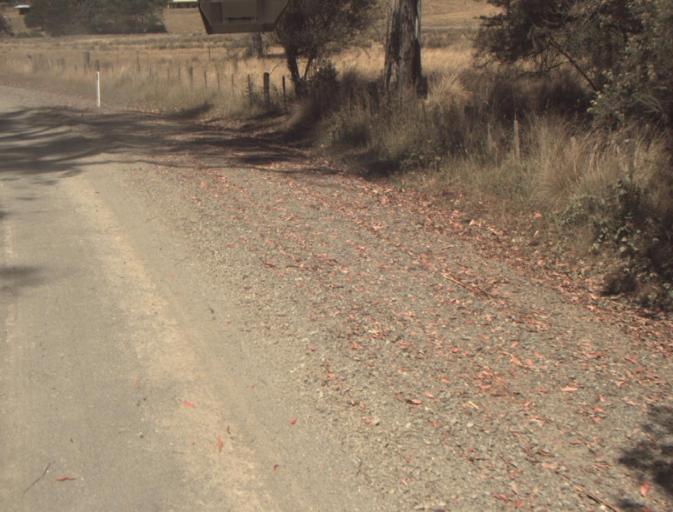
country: AU
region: Tasmania
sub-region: Dorset
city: Scottsdale
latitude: -41.2936
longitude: 147.3943
